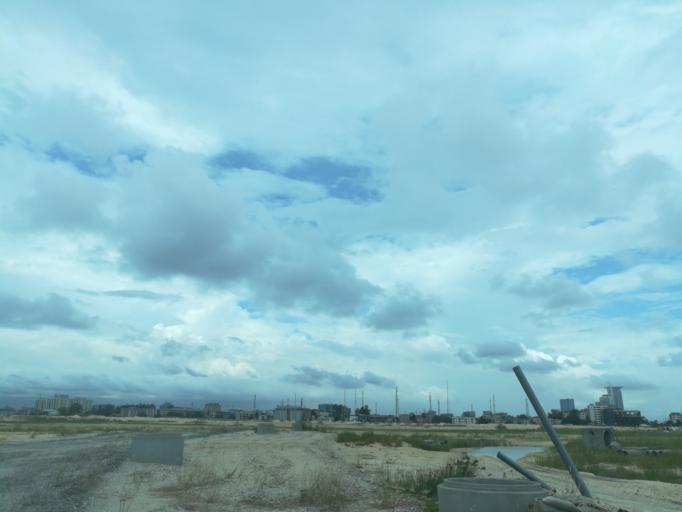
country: NG
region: Lagos
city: Ikoyi
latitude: 6.4162
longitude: 3.4230
